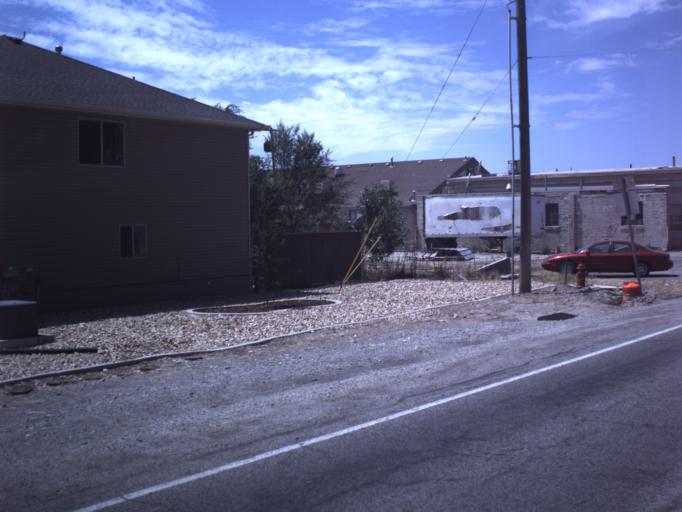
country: US
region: Utah
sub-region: Box Elder County
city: Elwood
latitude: 41.7124
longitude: -112.1409
